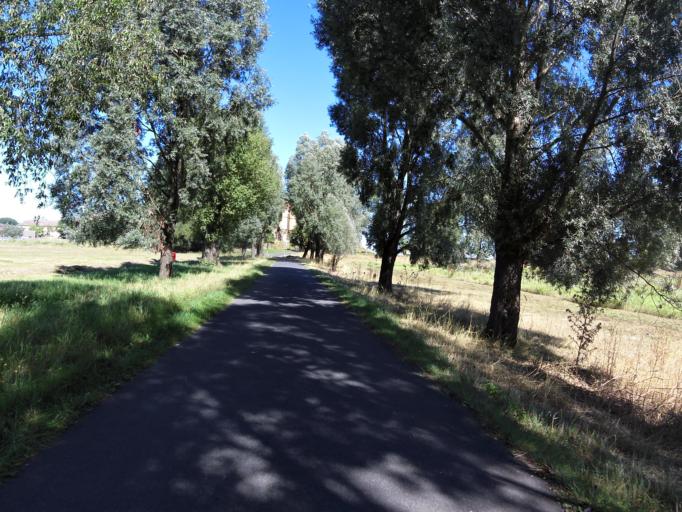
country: DE
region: Saxony-Anhalt
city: Pretzsch
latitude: 51.7128
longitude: 12.8152
